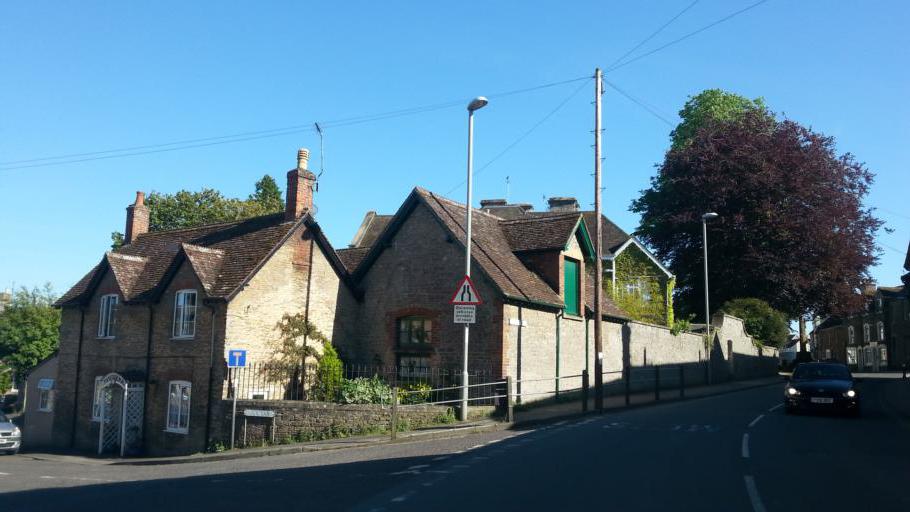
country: GB
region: England
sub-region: Dorset
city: Stalbridge
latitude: 50.9615
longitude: -2.3790
